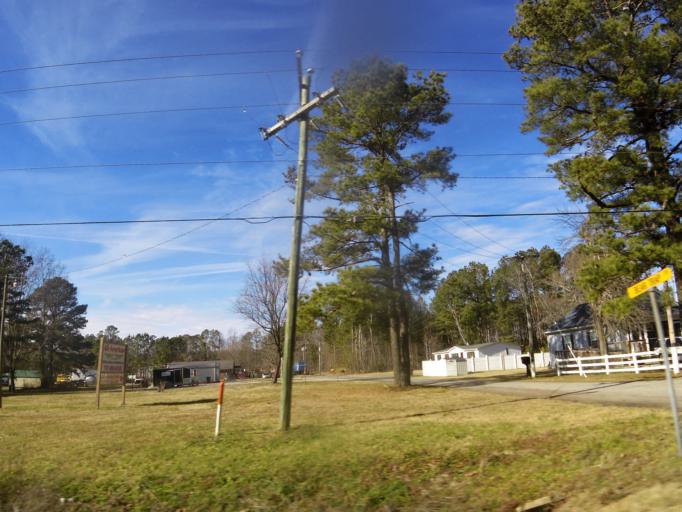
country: US
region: Virginia
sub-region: Isle of Wight County
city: Windsor
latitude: 36.8048
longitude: -76.7571
